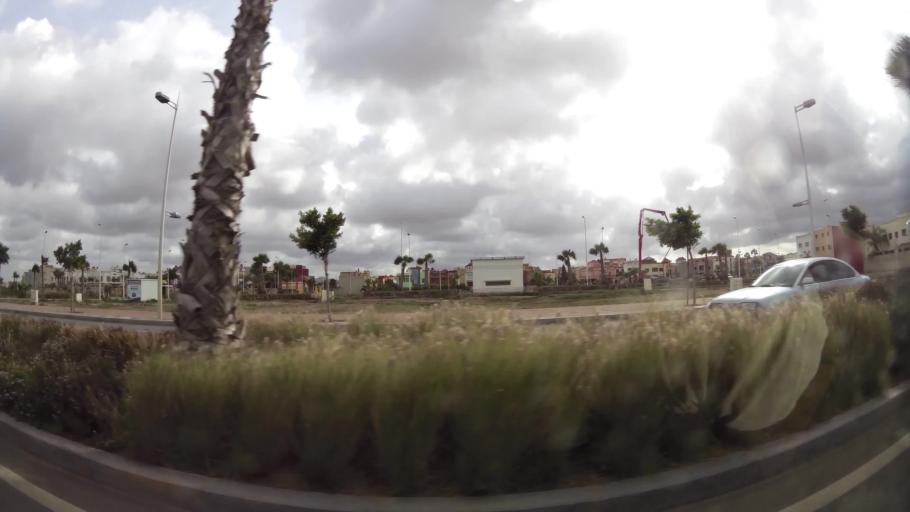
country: MA
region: Oriental
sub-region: Nador
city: Nador
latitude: 35.1664
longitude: -2.9125
